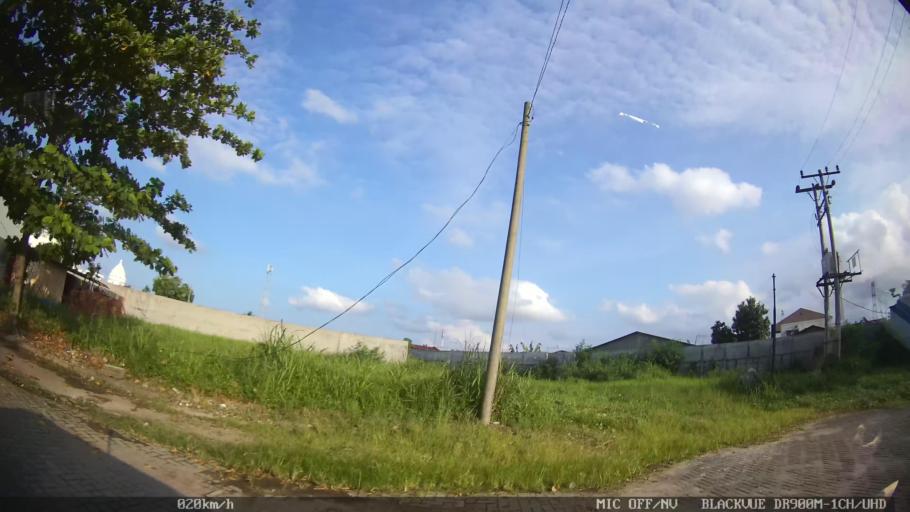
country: ID
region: North Sumatra
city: Medan
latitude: 3.6205
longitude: 98.6478
